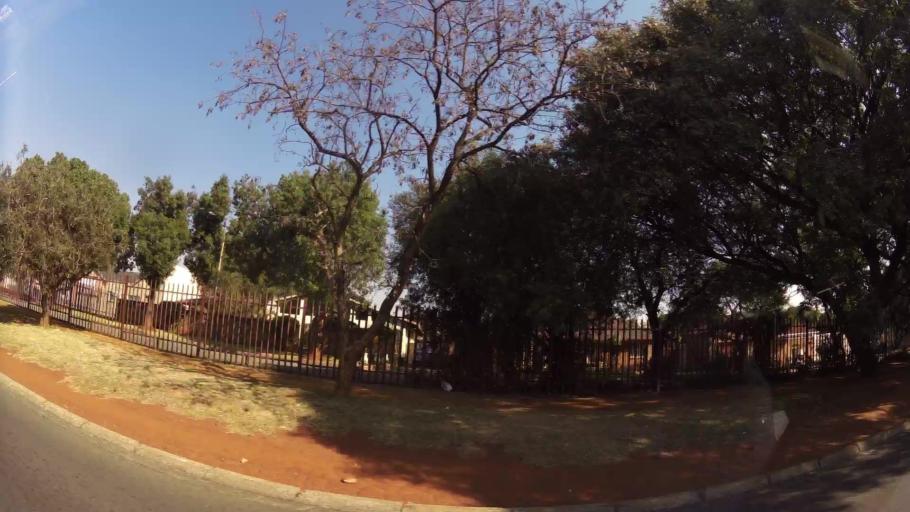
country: ZA
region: Gauteng
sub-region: Ekurhuleni Metropolitan Municipality
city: Boksburg
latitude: -26.2455
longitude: 28.2633
